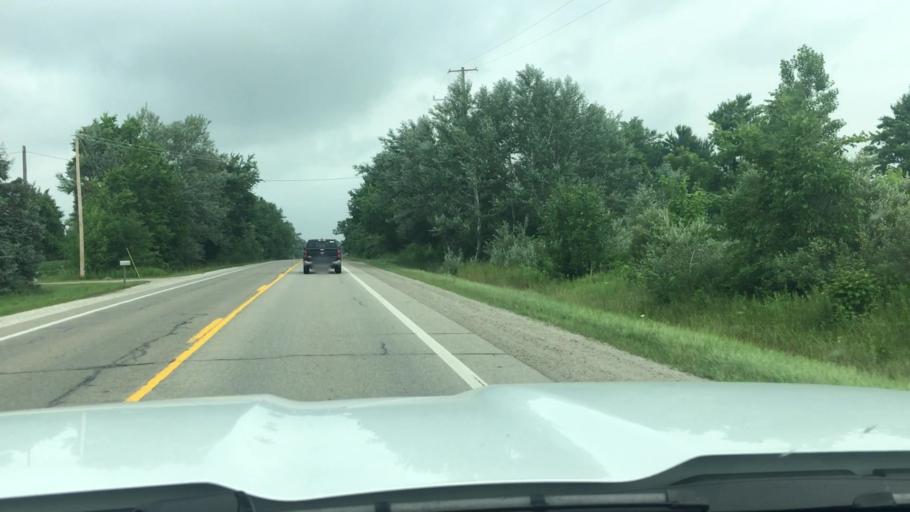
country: US
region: Michigan
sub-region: Sanilac County
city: Brown City
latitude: 43.1984
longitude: -83.0769
